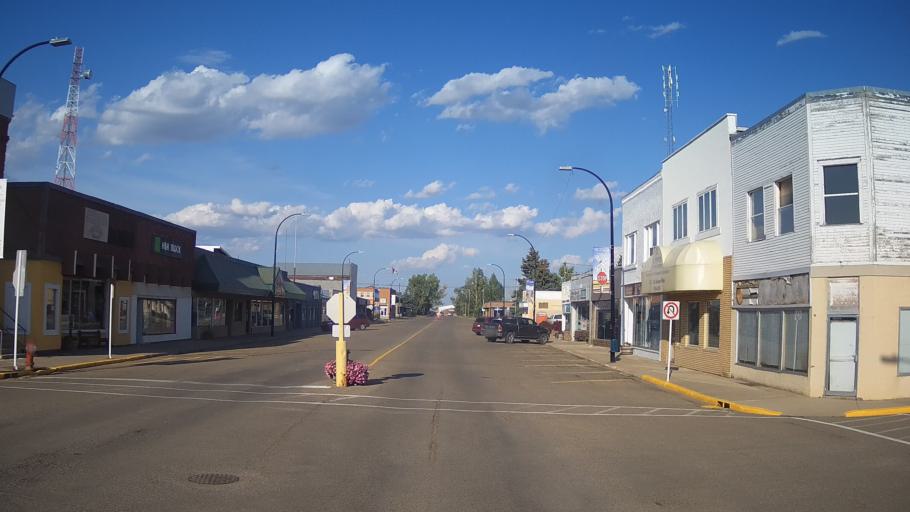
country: CA
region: Alberta
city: Hanna
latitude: 51.6430
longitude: -111.9280
